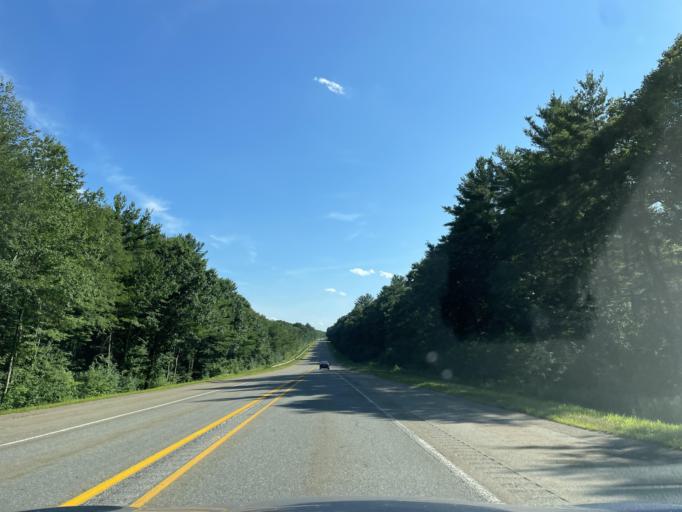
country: US
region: Massachusetts
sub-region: Worcester County
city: Sturbridge
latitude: 42.1509
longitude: -72.0374
